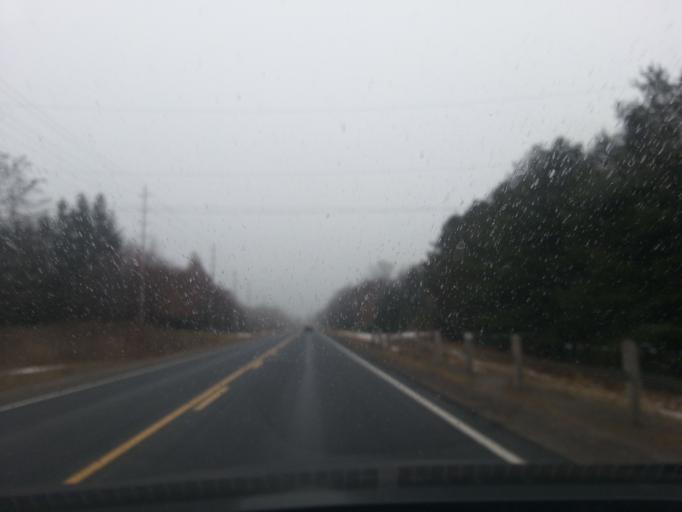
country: CA
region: Ontario
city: Omemee
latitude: 44.1955
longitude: -78.4856
